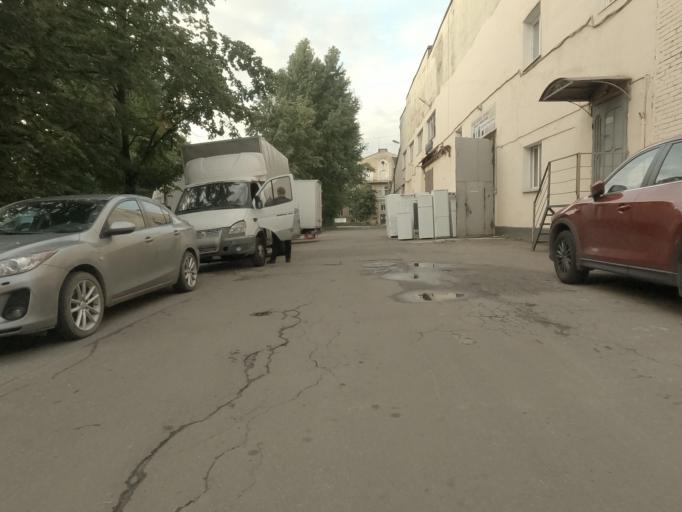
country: RU
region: St.-Petersburg
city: Avtovo
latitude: 59.8852
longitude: 30.2809
